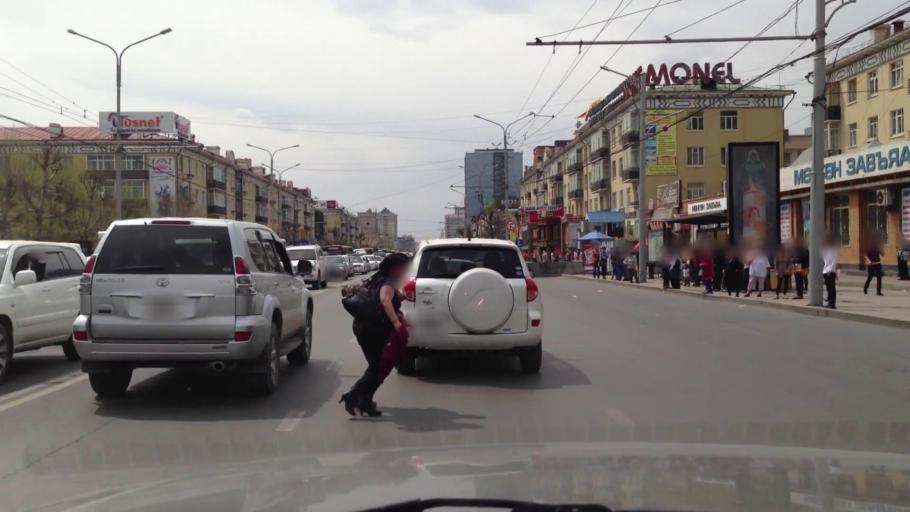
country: MN
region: Ulaanbaatar
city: Ulaanbaatar
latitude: 47.9165
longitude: 106.9096
